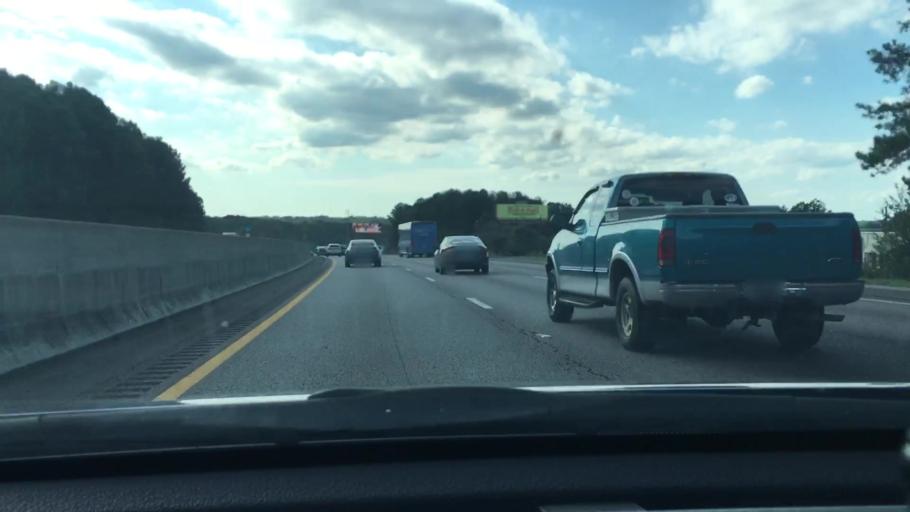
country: US
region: South Carolina
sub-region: Richland County
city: Columbia
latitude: 34.0664
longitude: -81.0365
